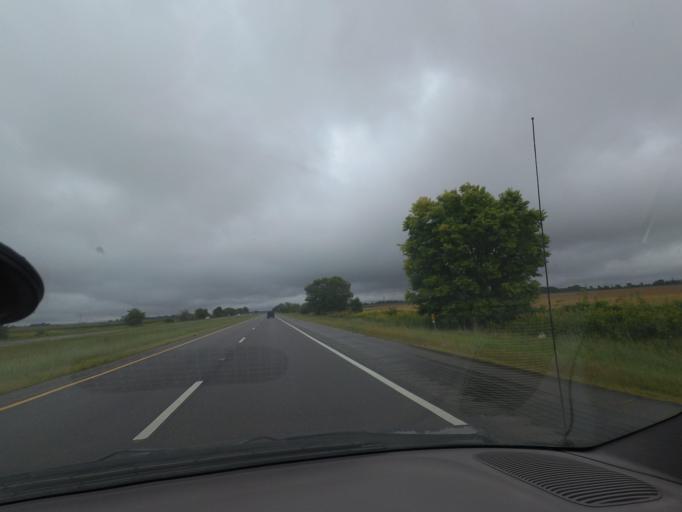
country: US
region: Illinois
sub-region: Champaign County
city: Lake of the Woods
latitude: 40.1206
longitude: -88.3531
